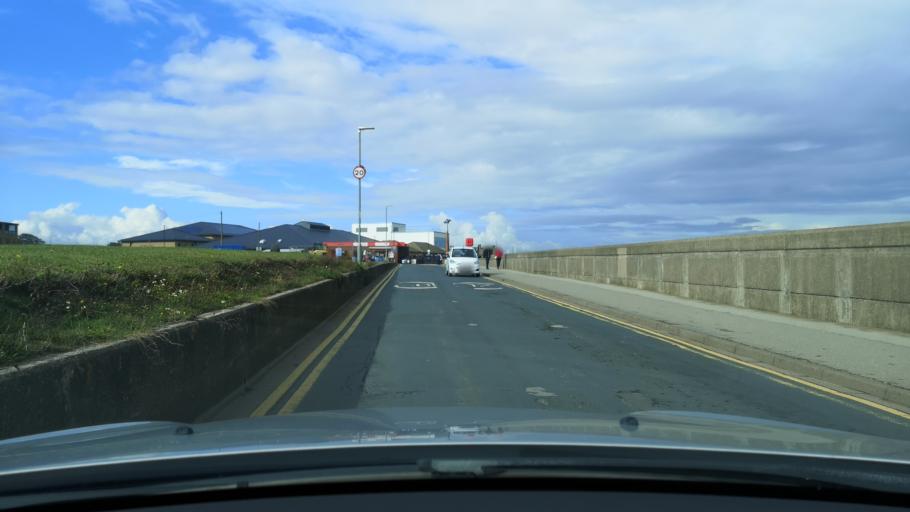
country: GB
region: England
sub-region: East Riding of Yorkshire
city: Hornsea
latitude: 53.9111
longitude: -0.1597
